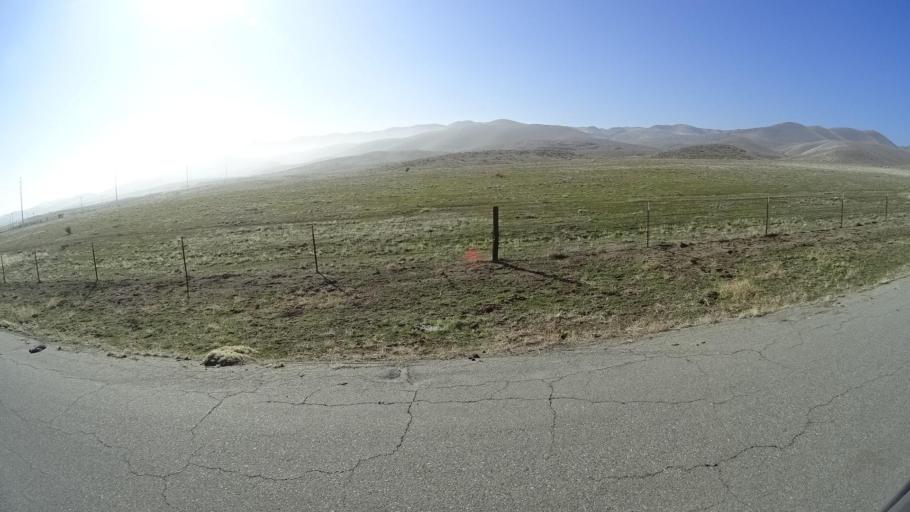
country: US
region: California
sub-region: Kern County
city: Taft Heights
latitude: 35.2279
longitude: -119.6366
